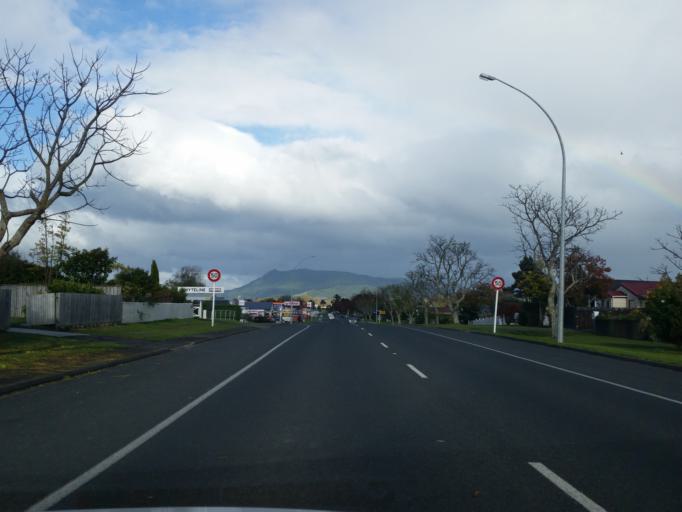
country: NZ
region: Waikato
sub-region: Hauraki District
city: Paeroa
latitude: -37.3710
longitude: 175.6628
